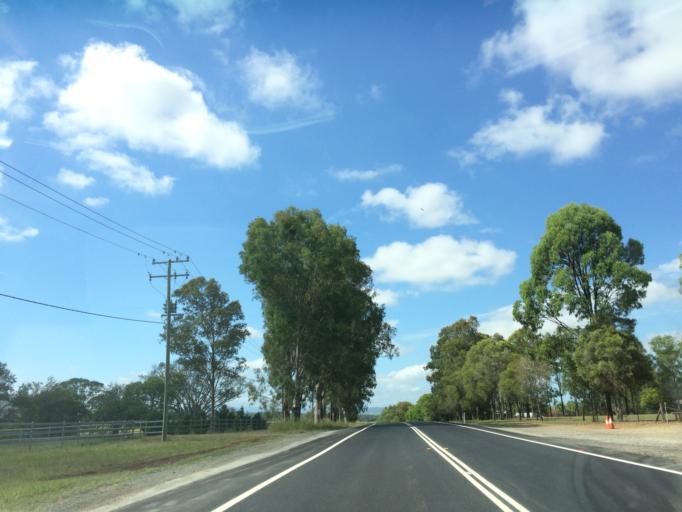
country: AU
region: Queensland
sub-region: Logan
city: Cedar Vale
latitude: -27.9001
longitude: 152.9748
